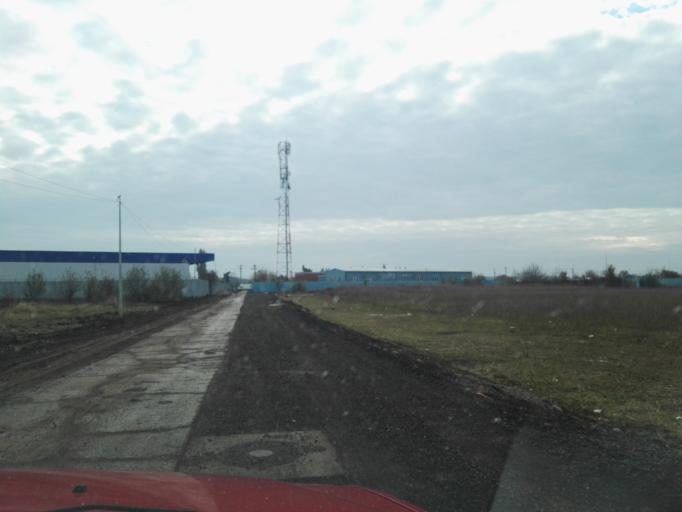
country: RO
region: Ilfov
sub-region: Comuna Magurele
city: Magurele
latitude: 44.3765
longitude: 26.0433
